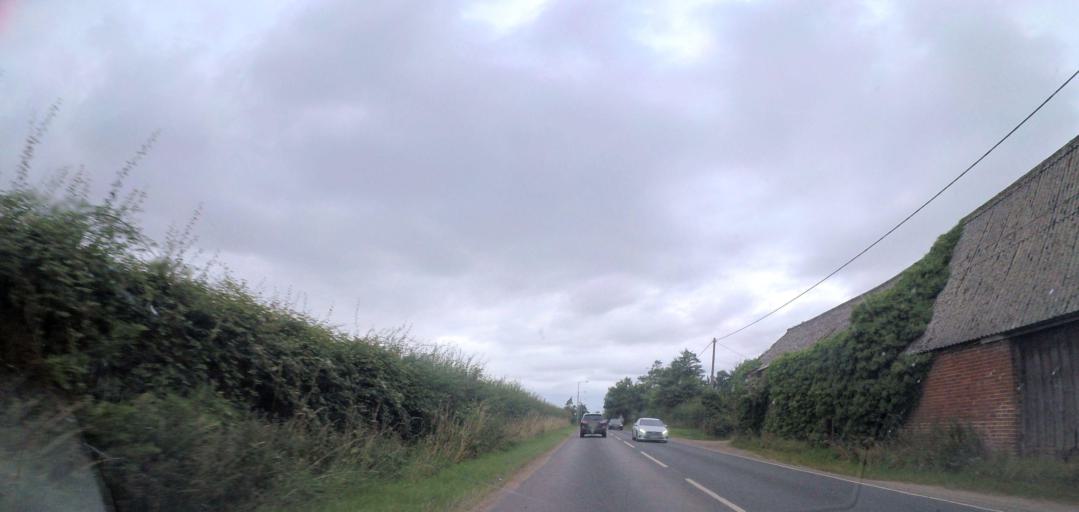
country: GB
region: England
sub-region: Norfolk
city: Coltishall
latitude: 52.7200
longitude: 1.3505
